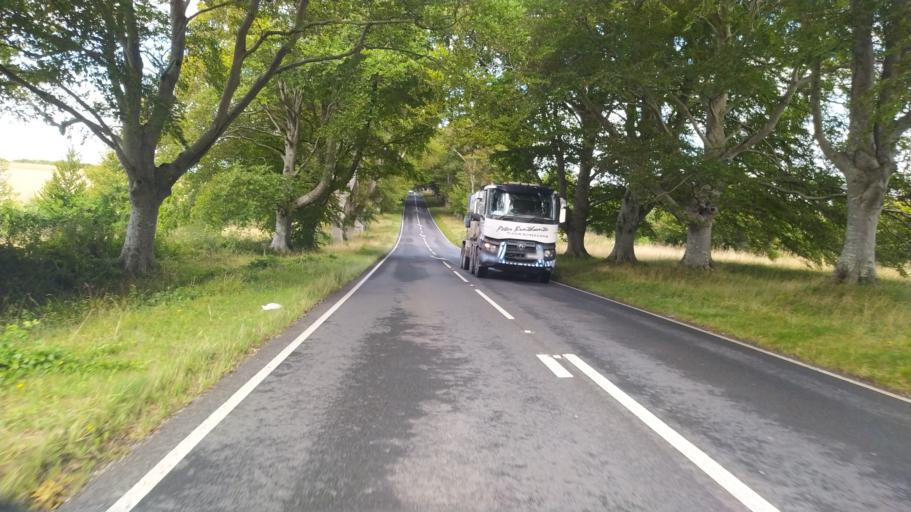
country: GB
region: England
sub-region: Dorset
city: Lytchett Matravers
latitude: 50.8297
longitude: -2.0709
